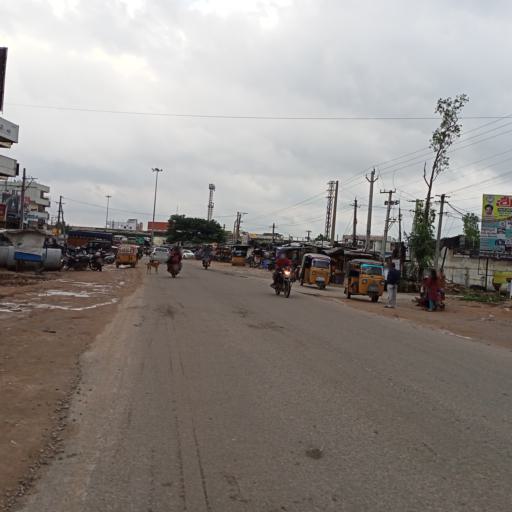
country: IN
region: Telangana
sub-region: Mahbubnagar
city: Mahbubnagar
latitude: 16.7741
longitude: 78.1297
